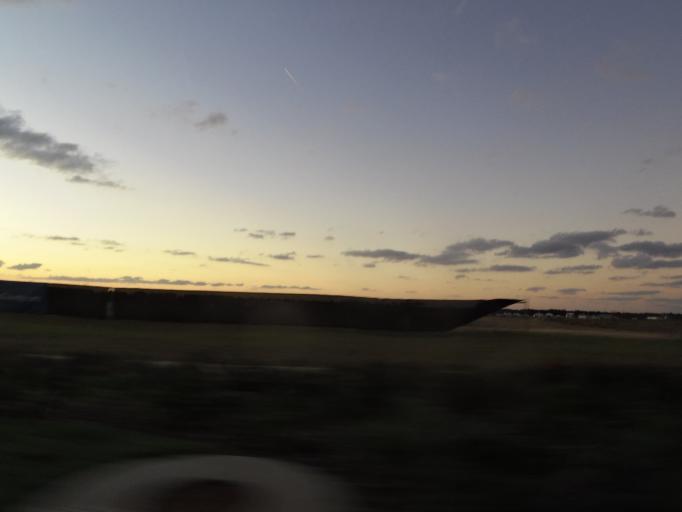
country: US
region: Florida
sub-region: Saint Johns County
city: Palm Valley
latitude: 30.0782
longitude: -81.4813
